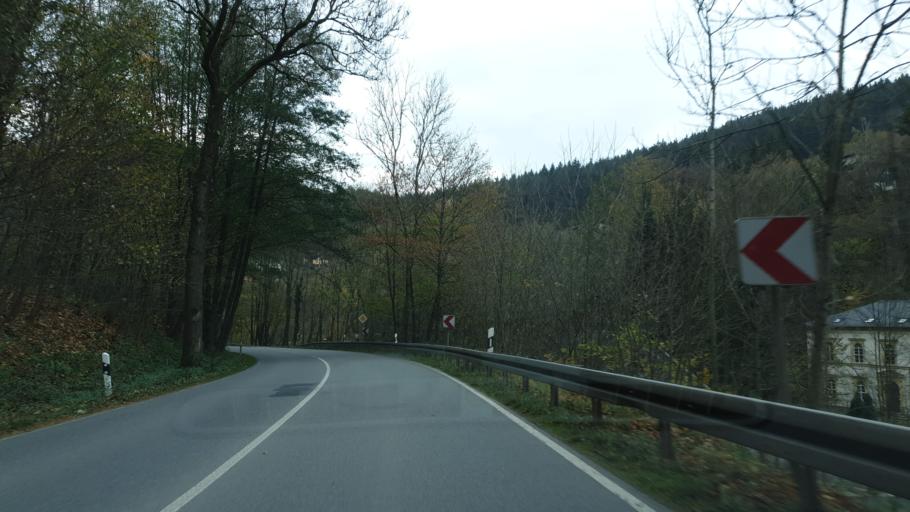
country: DE
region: Saxony
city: Schwarzenberg
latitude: 50.5157
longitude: 12.7765
